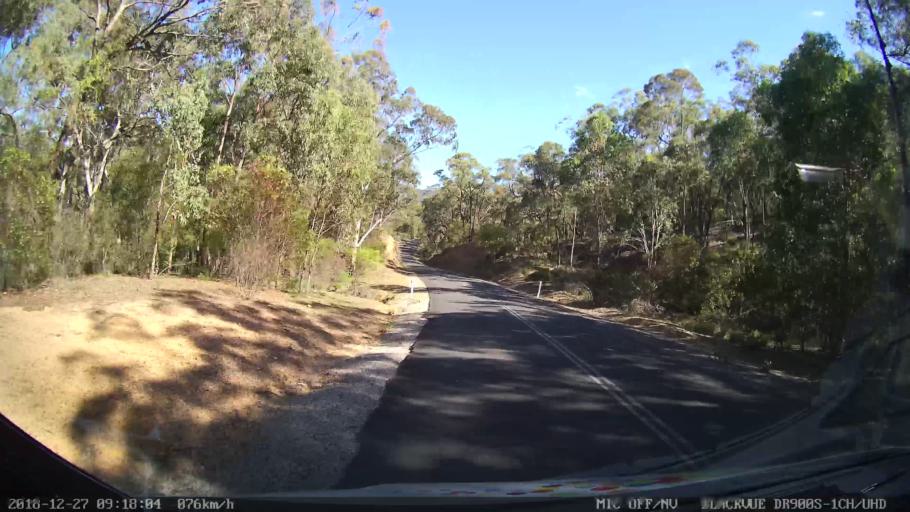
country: AU
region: New South Wales
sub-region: Lithgow
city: Portland
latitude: -33.1309
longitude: 150.0460
